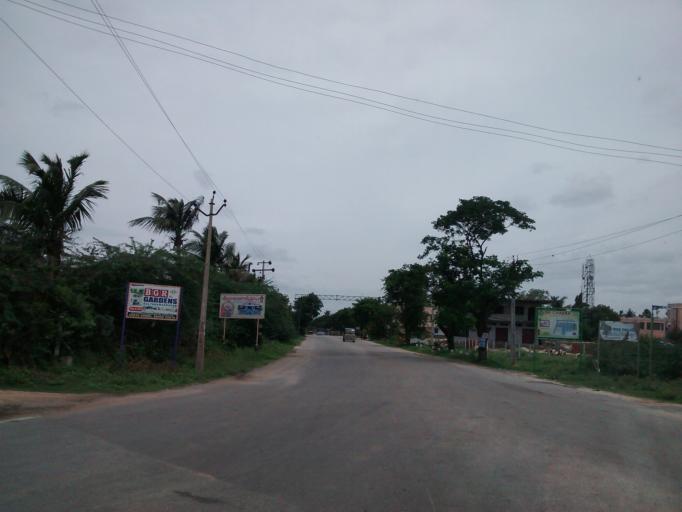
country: IN
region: Andhra Pradesh
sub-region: Chittoor
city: Narasingapuram
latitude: 13.6109
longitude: 79.3325
